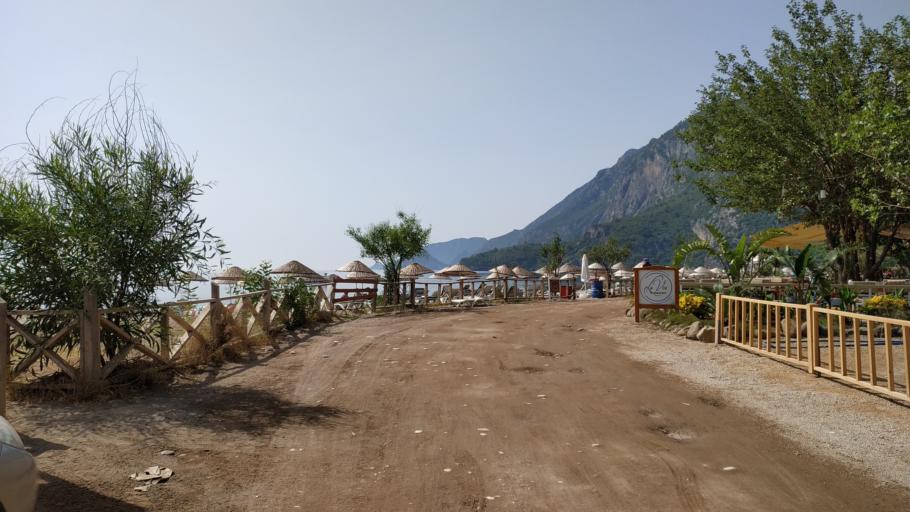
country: TR
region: Antalya
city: Tekirova
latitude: 36.4057
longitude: 30.4781
